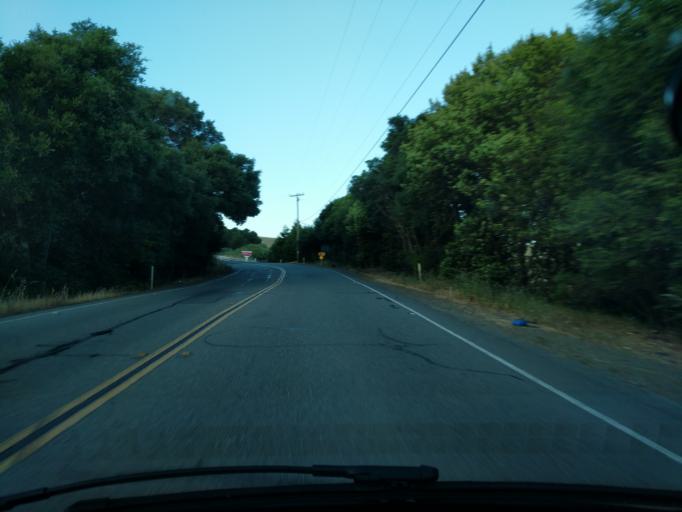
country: US
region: California
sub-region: Contra Costa County
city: San Ramon
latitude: 37.7680
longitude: -122.0080
